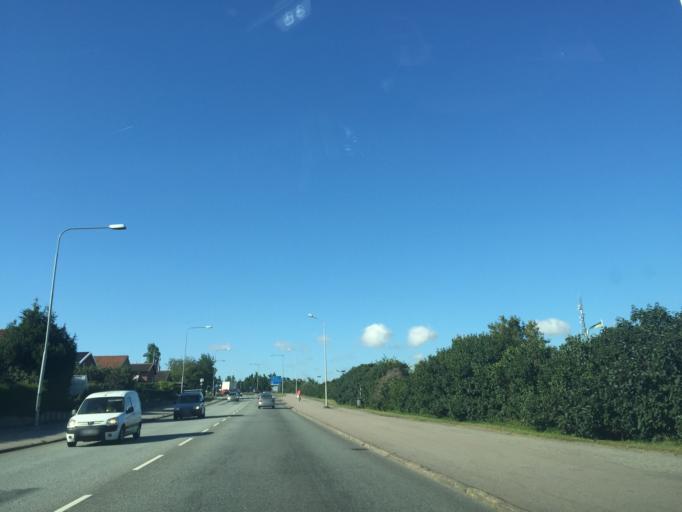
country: SE
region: Skane
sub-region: Ystads Kommun
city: Ystad
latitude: 55.4406
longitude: 13.8354
